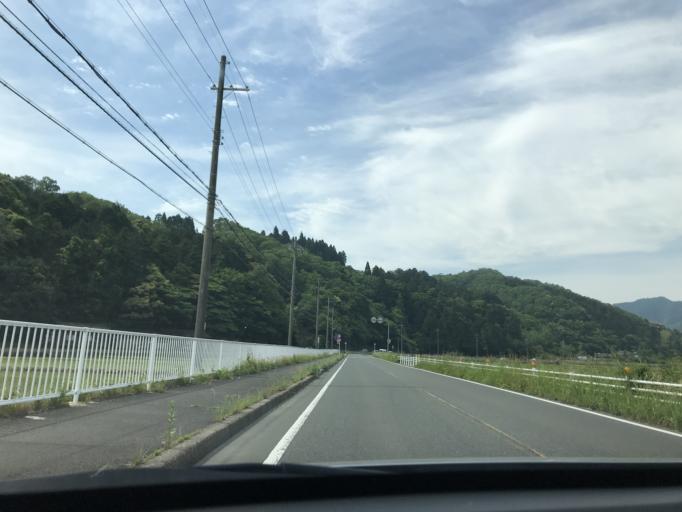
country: JP
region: Kyoto
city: Miyazu
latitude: 35.6644
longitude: 135.0236
